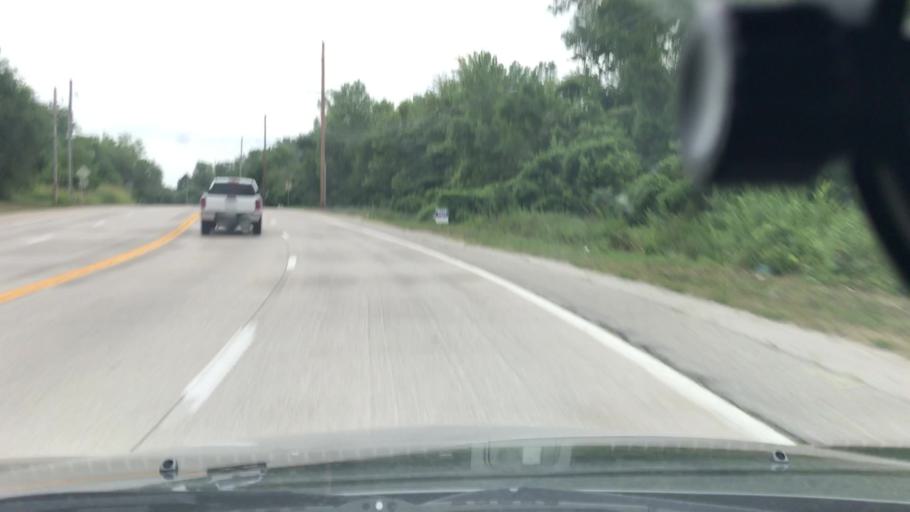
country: US
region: Missouri
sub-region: Saint Charles County
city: Saint Charles
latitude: 38.7431
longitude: -90.5179
